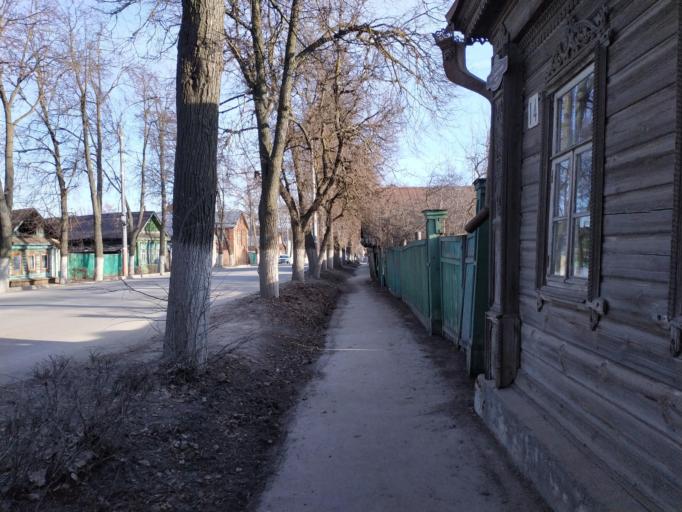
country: RU
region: Nizjnij Novgorod
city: Arzamas
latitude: 55.3934
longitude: 43.8120
